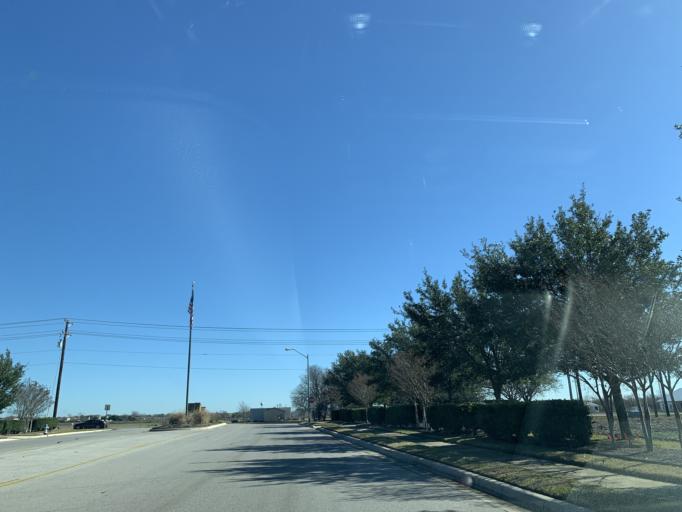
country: US
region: Texas
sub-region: Williamson County
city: Hutto
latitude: 30.5476
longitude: -97.5619
